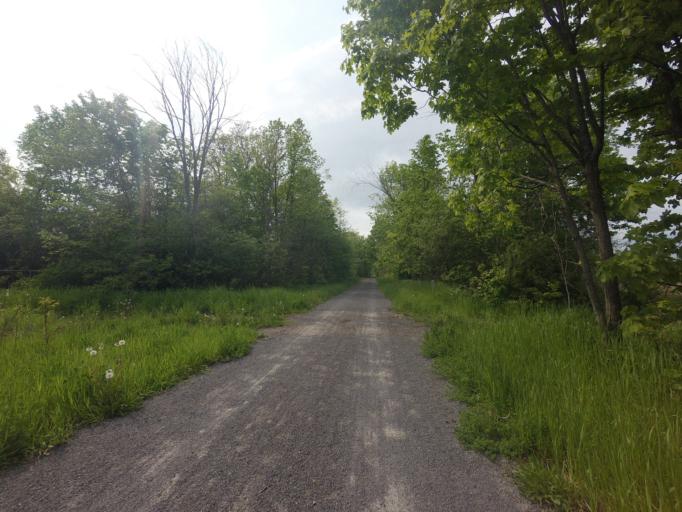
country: CA
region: Ontario
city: Kingston
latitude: 44.3451
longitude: -76.6053
